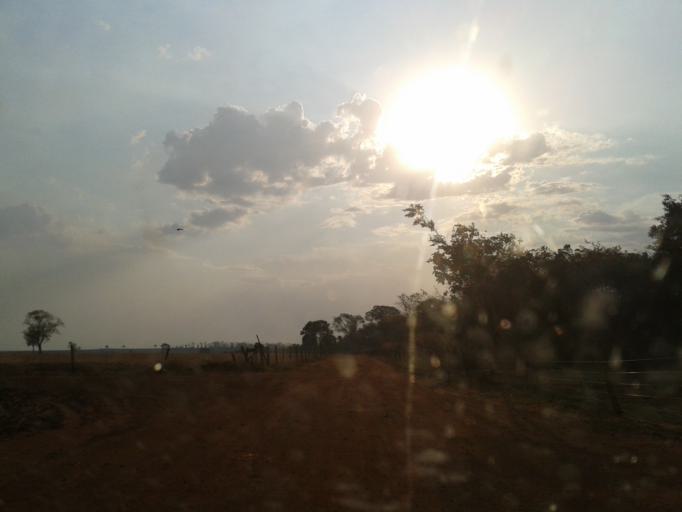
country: BR
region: Minas Gerais
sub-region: Capinopolis
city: Capinopolis
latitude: -18.7560
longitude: -49.7098
